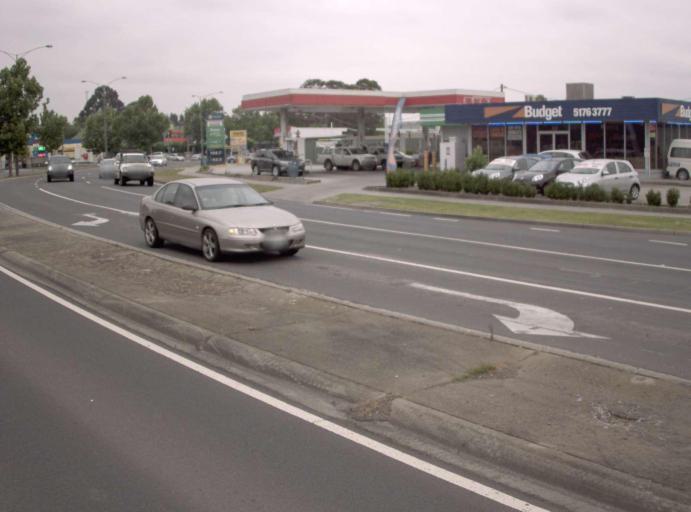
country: AU
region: Victoria
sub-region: Latrobe
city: Traralgon
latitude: -38.1967
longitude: 146.5411
